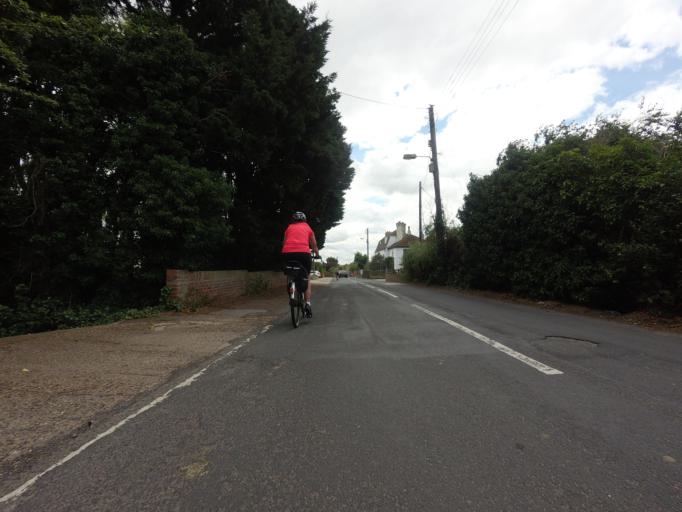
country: GB
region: England
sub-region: Medway
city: Allhallows
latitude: 51.4548
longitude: 0.6352
